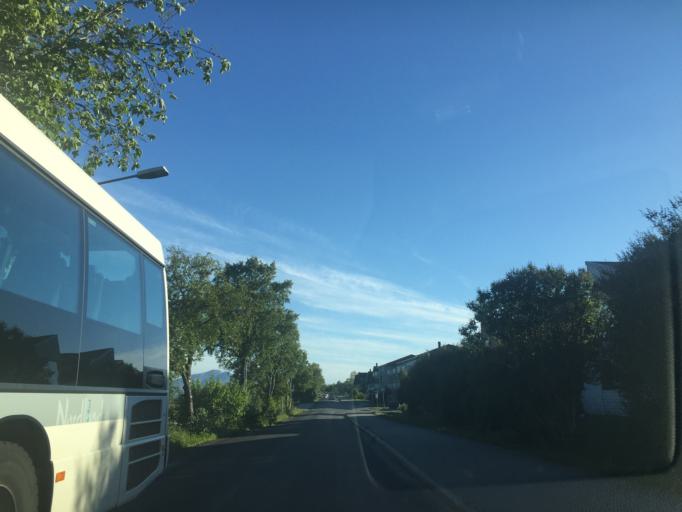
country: NO
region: Nordland
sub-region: Bodo
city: Lopsmarka
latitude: 67.2911
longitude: 14.4538
